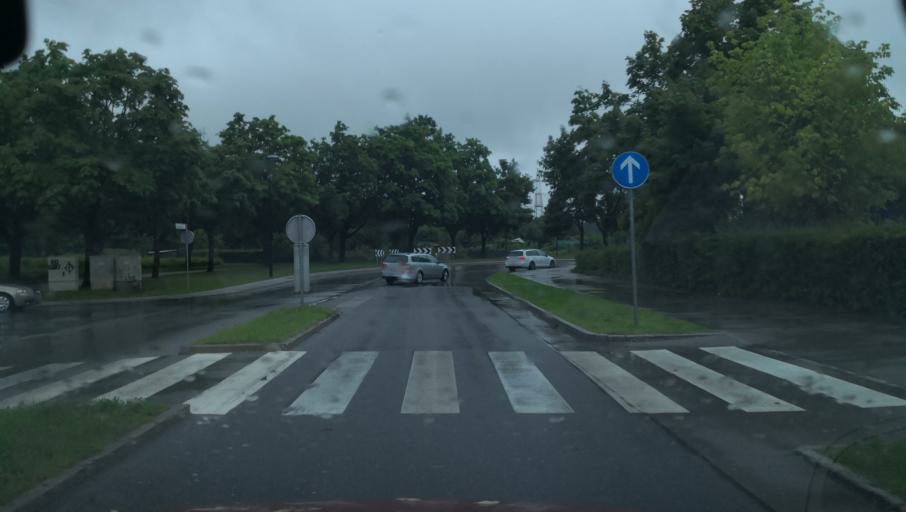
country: SI
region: Ljubljana
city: Ljubljana
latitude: 46.0824
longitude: 14.4931
